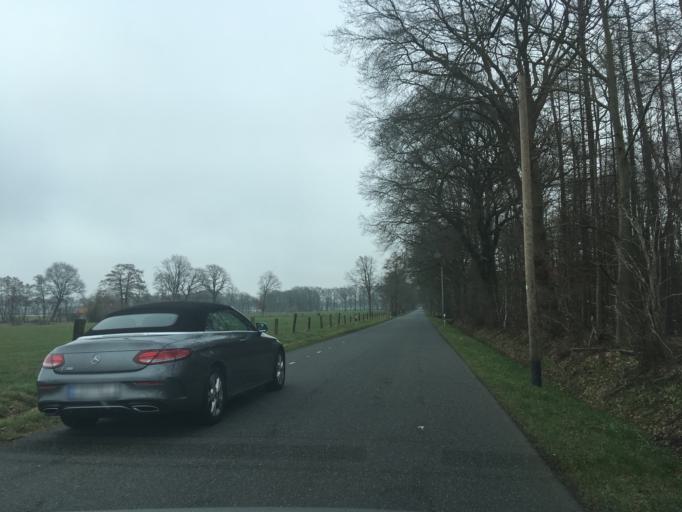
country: DE
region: North Rhine-Westphalia
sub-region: Regierungsbezirk Munster
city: Rhede
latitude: 51.8859
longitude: 6.6937
